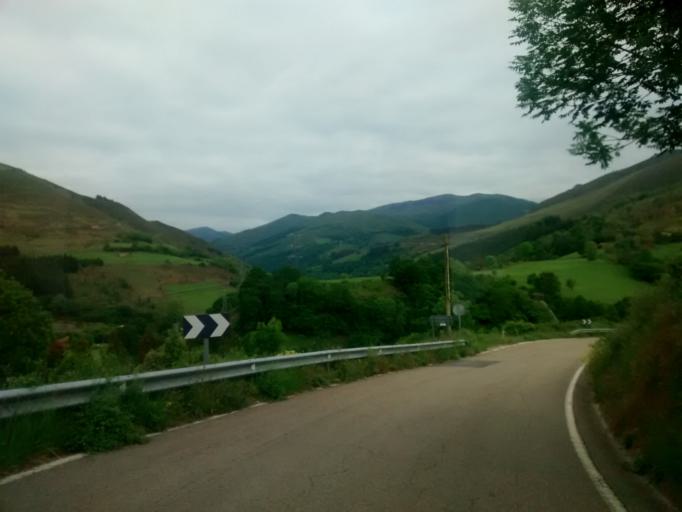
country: ES
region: Cantabria
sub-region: Provincia de Cantabria
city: San Vicente de la Barquera
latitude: 43.2536
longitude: -4.4148
